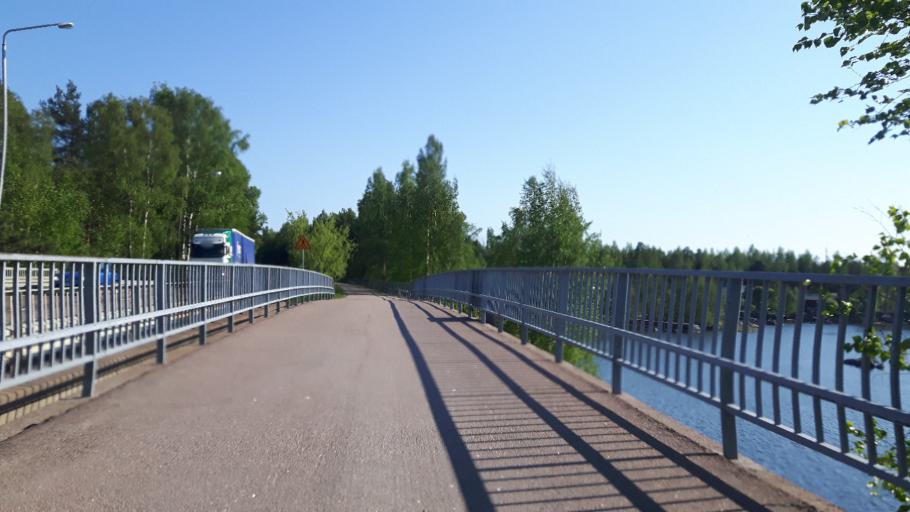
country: FI
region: Kymenlaakso
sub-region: Kotka-Hamina
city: Kotka
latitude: 60.4689
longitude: 26.8780
